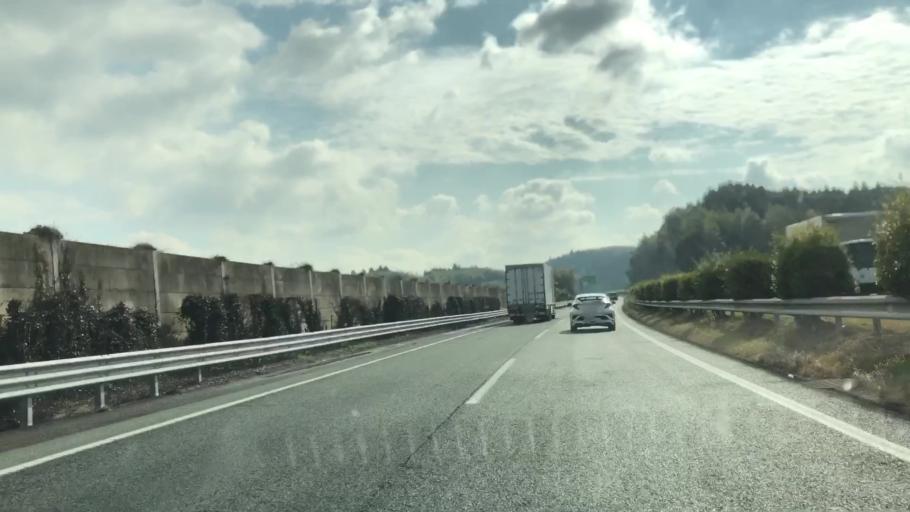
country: JP
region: Fukuoka
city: Setakamachi-takayanagi
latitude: 33.0838
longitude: 130.5417
